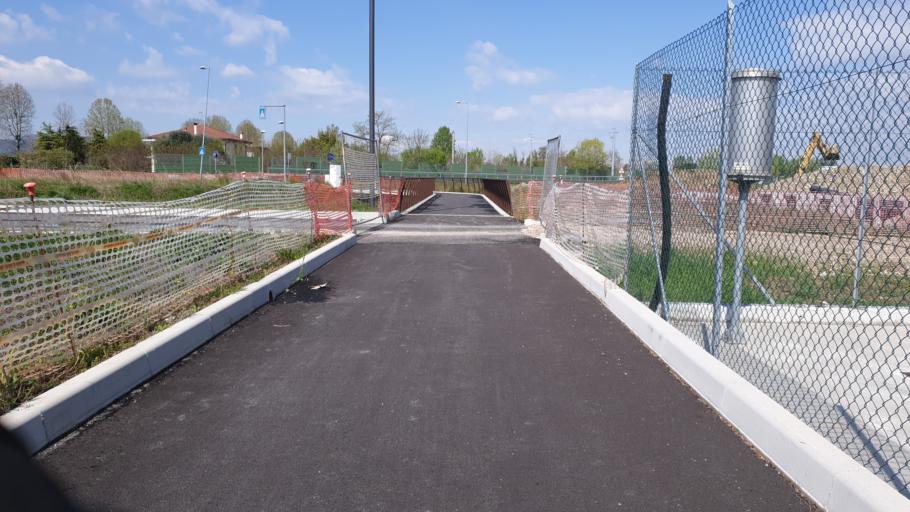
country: IT
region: Veneto
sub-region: Provincia di Padova
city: Abano Terme
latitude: 45.3600
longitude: 11.8115
